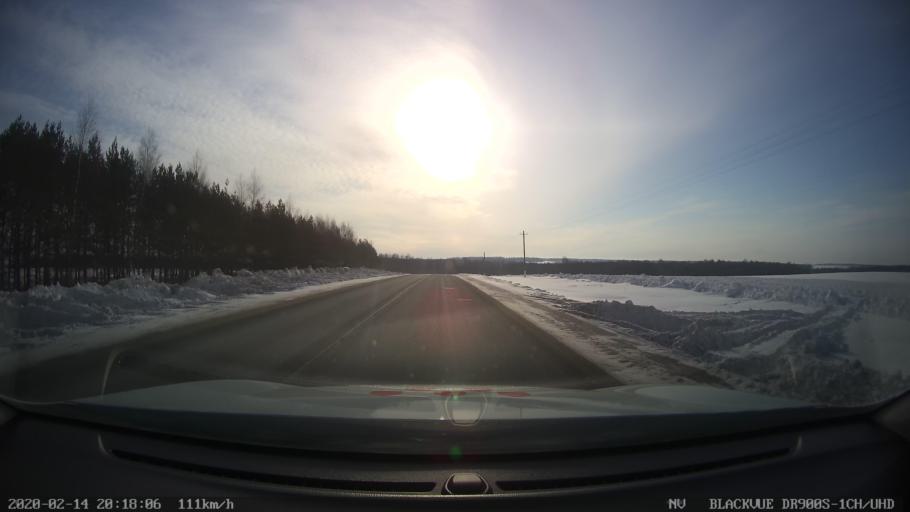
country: RU
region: Tatarstan
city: Verkhniy Uslon
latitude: 55.5909
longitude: 48.8845
